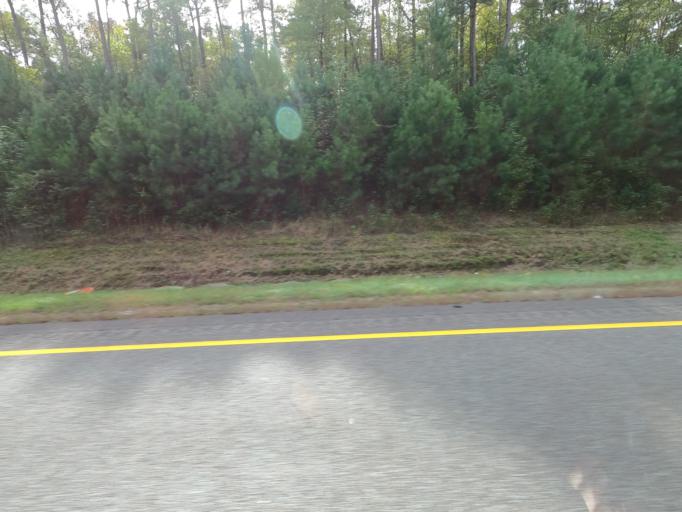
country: US
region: Tennessee
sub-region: Decatur County
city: Parsons
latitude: 35.8162
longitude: -88.2238
